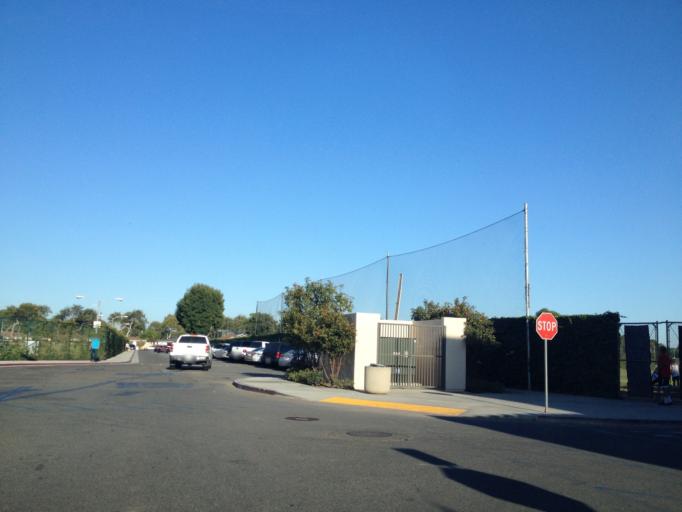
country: US
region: California
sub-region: Orange County
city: Fullerton
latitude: 33.8772
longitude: -117.9167
